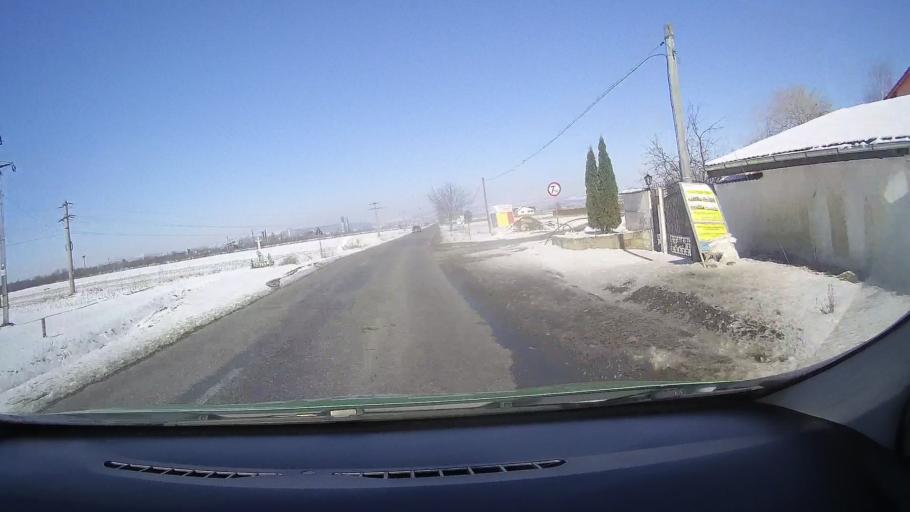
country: RO
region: Brasov
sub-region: Comuna Harseni
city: Harseni
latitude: 45.7941
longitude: 24.9952
